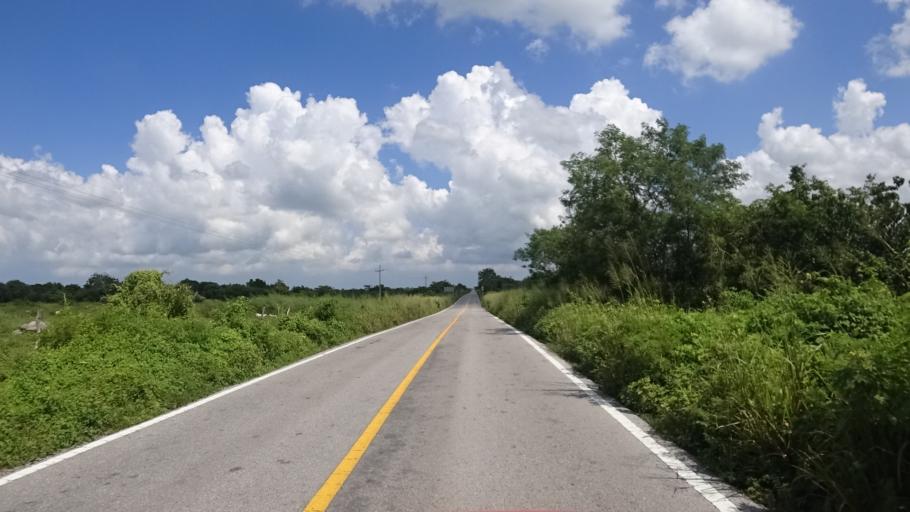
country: MX
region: Yucatan
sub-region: Panaba
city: Loche
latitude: 21.4657
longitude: -88.1316
